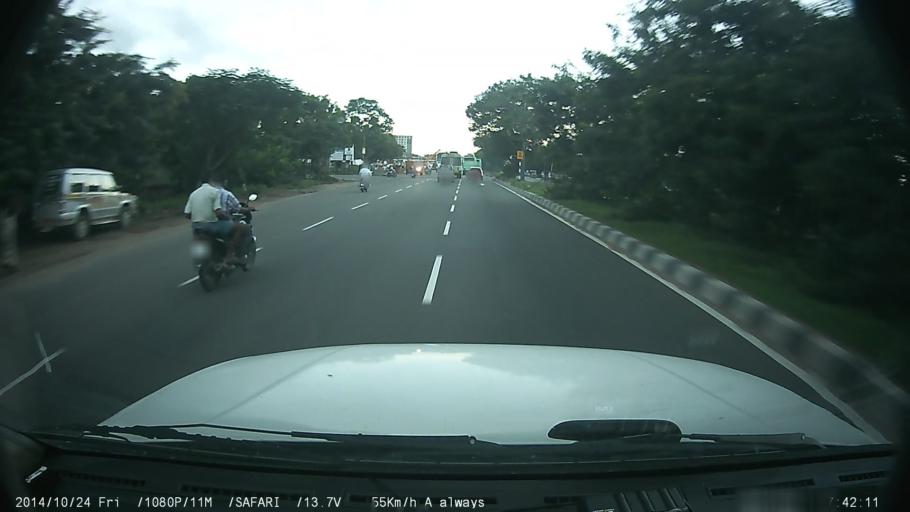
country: IN
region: Tamil Nadu
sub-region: Kancheepuram
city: Singapperumalkovil
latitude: 12.7719
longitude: 80.0080
